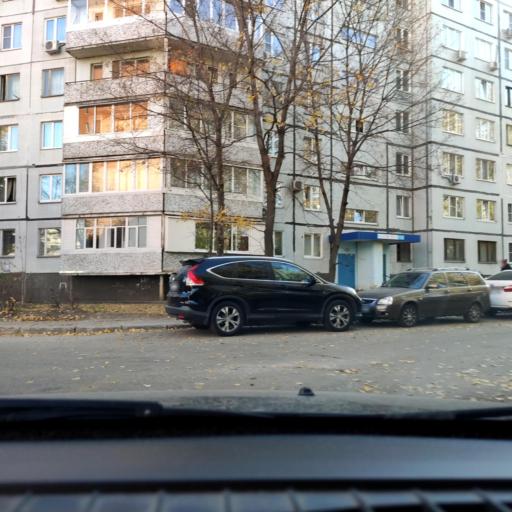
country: RU
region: Samara
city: Tol'yatti
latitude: 53.5211
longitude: 49.3013
